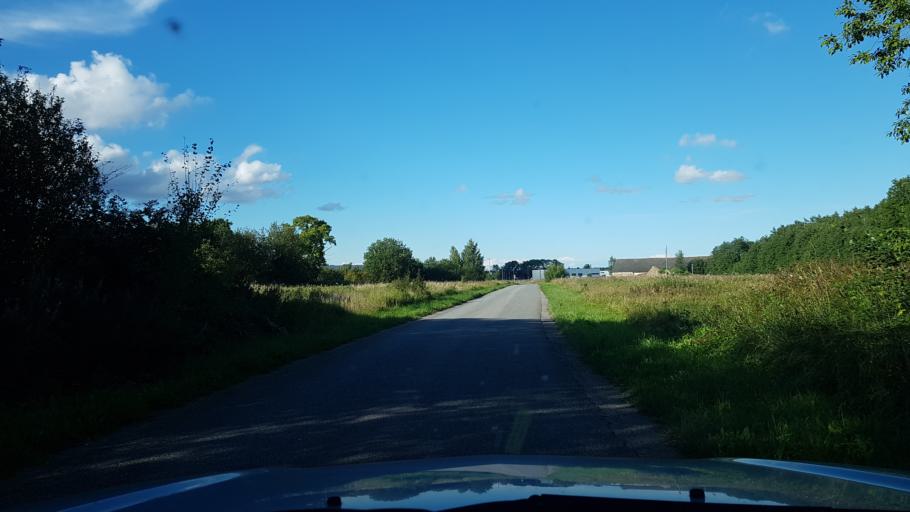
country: EE
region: Harju
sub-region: Kiili vald
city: Kiili
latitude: 59.3312
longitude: 24.8326
